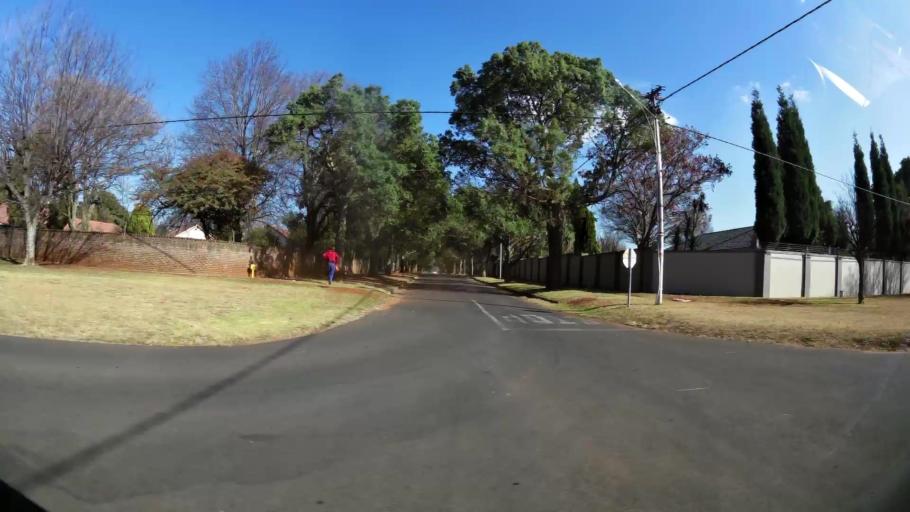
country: ZA
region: Gauteng
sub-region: Ekurhuleni Metropolitan Municipality
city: Benoni
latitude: -26.1505
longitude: 28.3326
